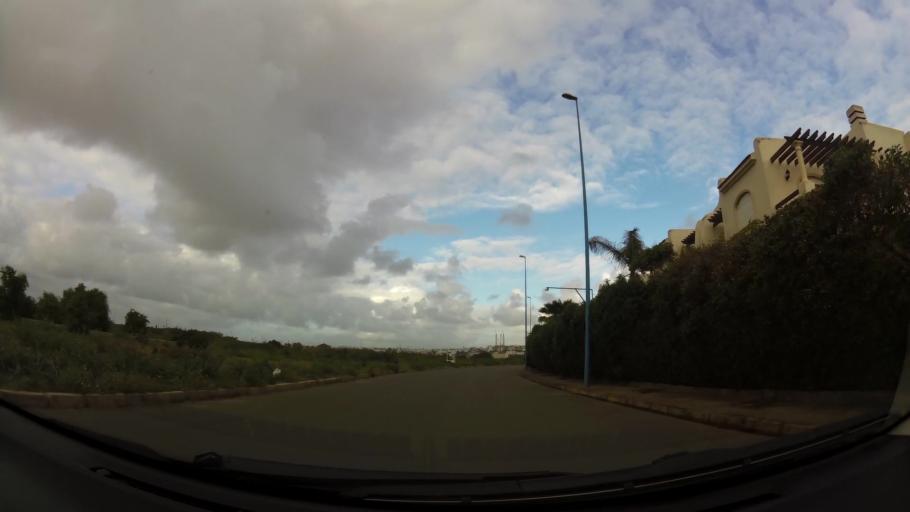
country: MA
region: Grand Casablanca
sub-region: Casablanca
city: Casablanca
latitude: 33.5789
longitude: -7.6982
